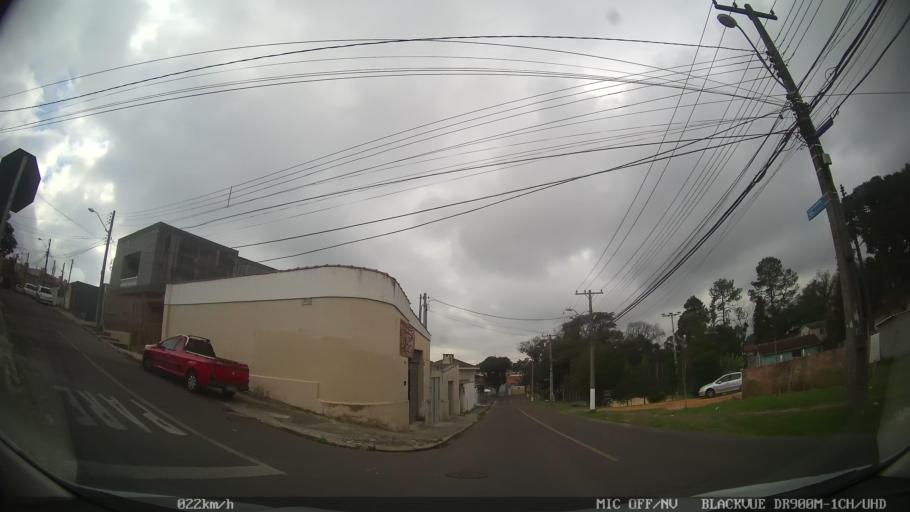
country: BR
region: Parana
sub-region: Curitiba
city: Curitiba
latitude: -25.3789
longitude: -49.2604
